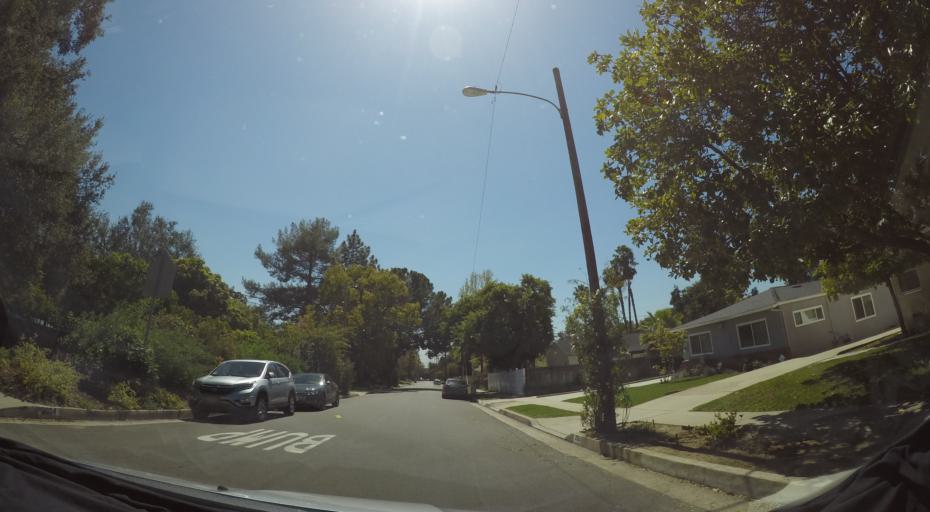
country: US
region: California
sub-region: Los Angeles County
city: Altadena
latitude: 34.1809
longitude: -118.1286
